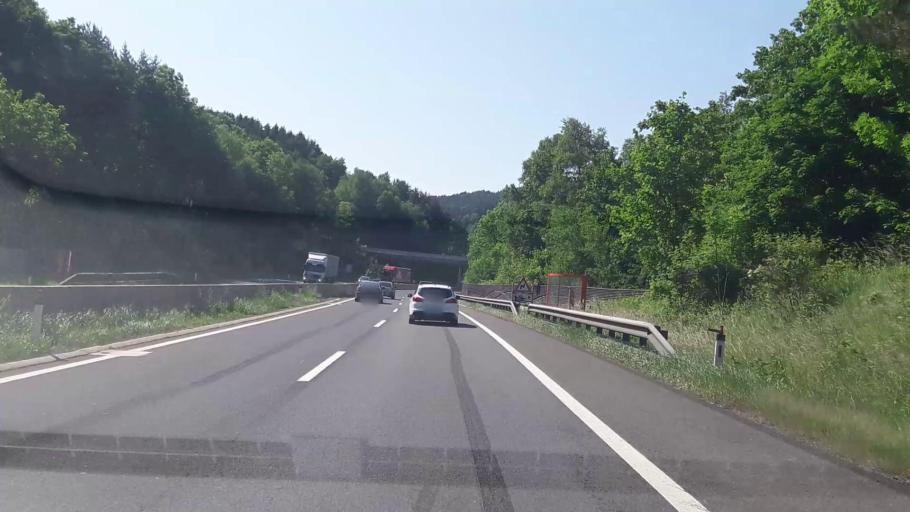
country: AT
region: Lower Austria
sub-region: Politischer Bezirk Neunkirchen
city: Grimmenstein
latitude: 47.6082
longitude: 16.1293
